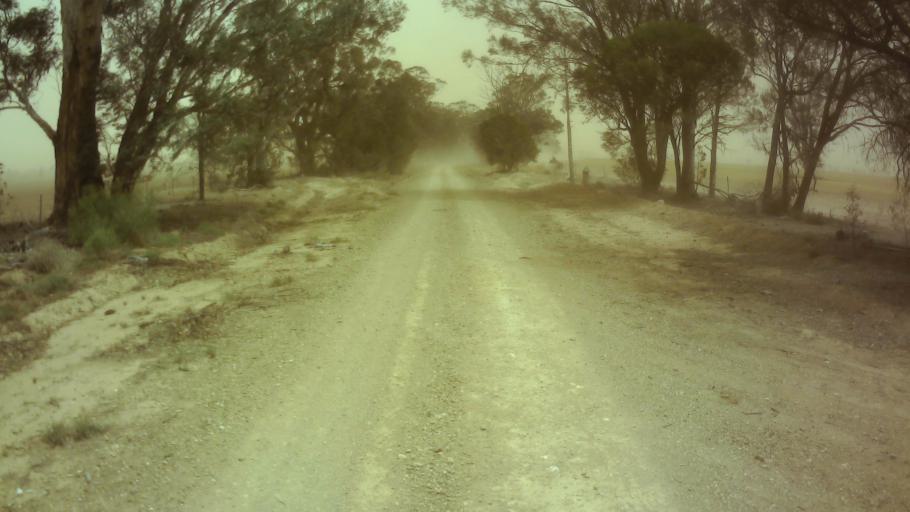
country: AU
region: New South Wales
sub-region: Weddin
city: Grenfell
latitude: -33.7079
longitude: 147.9378
